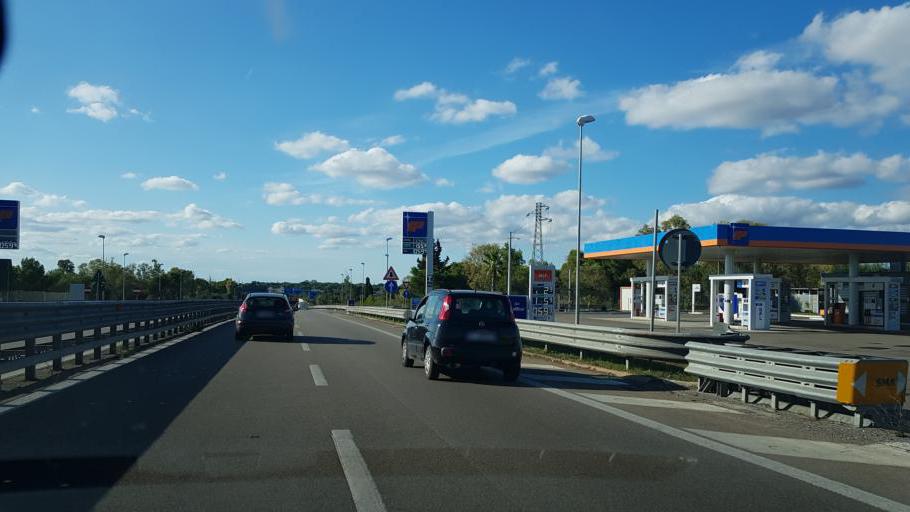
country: IT
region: Apulia
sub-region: Provincia di Lecce
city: Lequile
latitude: 40.3313
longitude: 18.1379
